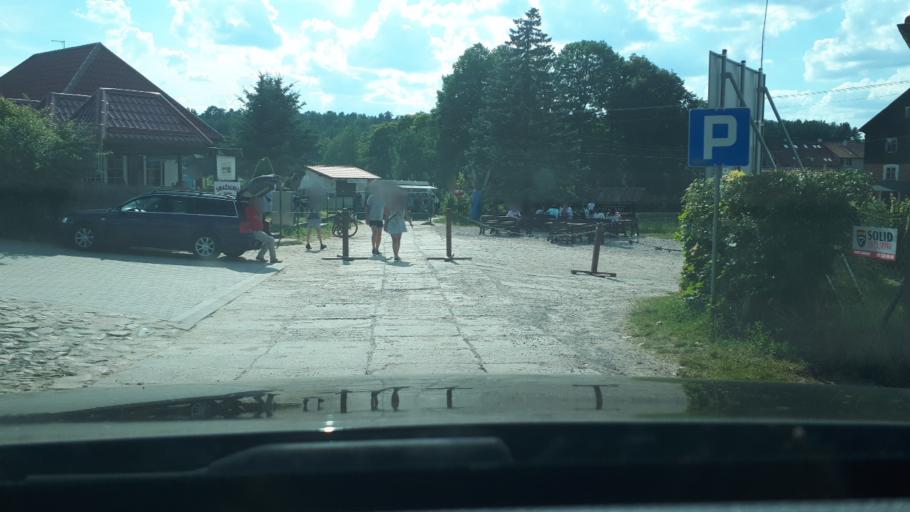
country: PL
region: Warmian-Masurian Voivodeship
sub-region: Powiat olsztynski
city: Stawiguda
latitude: 53.5483
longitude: 20.4183
